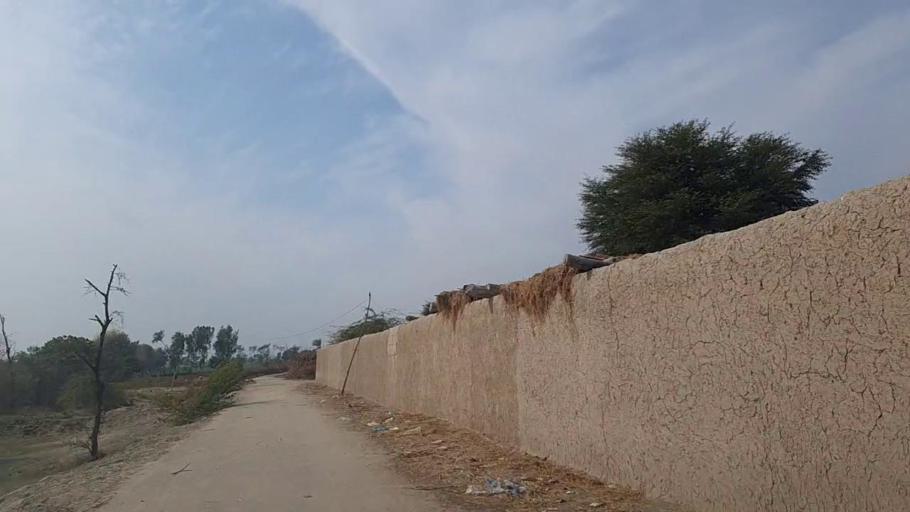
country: PK
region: Sindh
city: Daur
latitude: 26.5006
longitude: 68.3975
